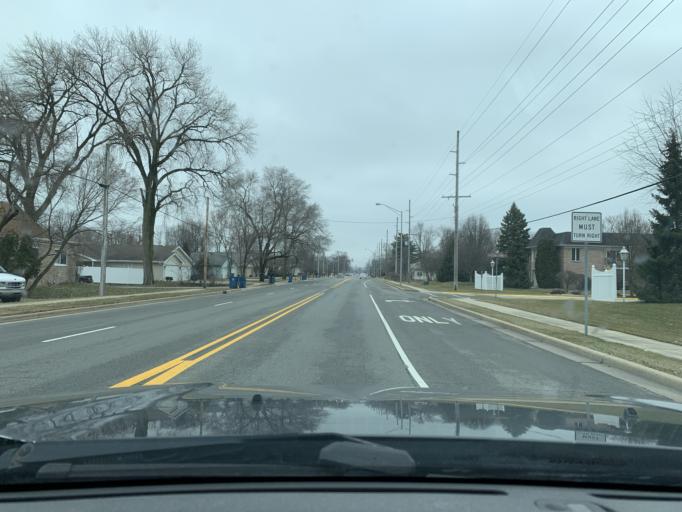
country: US
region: Indiana
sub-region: Lake County
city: Highland
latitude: 41.5364
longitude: -87.4616
